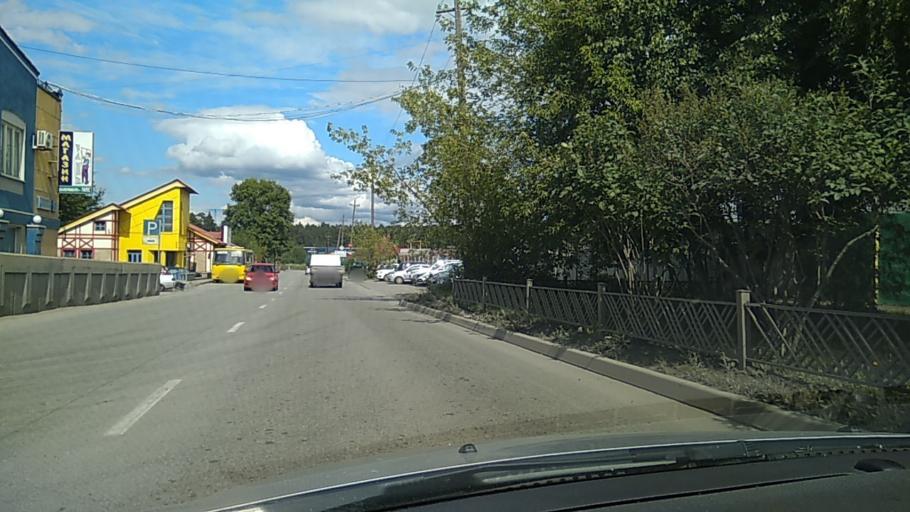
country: RU
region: Sverdlovsk
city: Shuvakish
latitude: 56.8863
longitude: 60.5355
